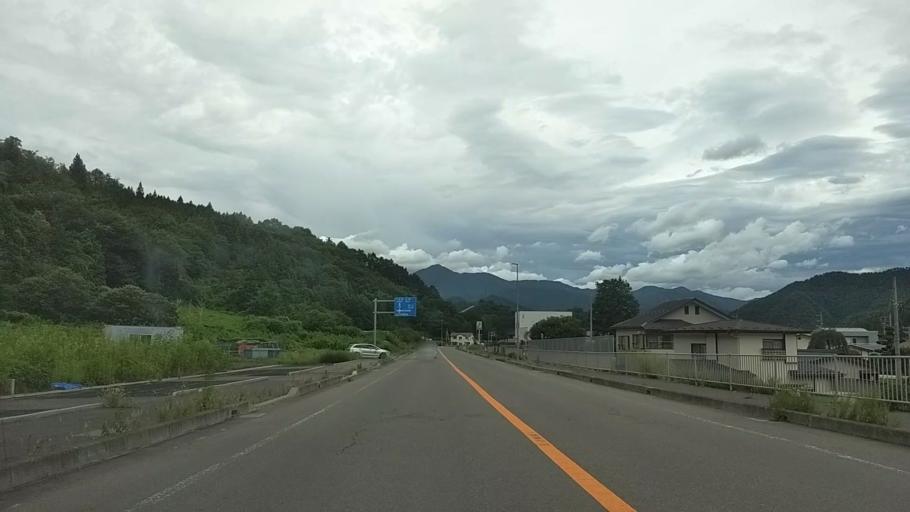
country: JP
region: Yamanashi
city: Otsuki
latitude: 35.5670
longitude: 138.9320
